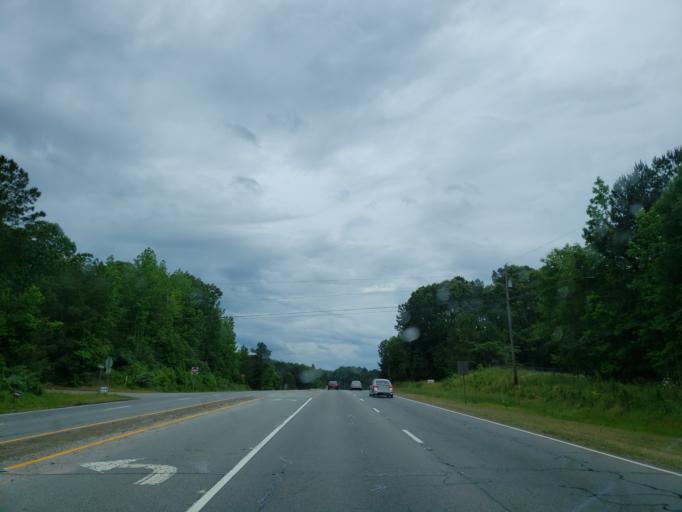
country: US
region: Georgia
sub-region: Haralson County
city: Bremen
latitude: 33.7591
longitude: -85.1630
